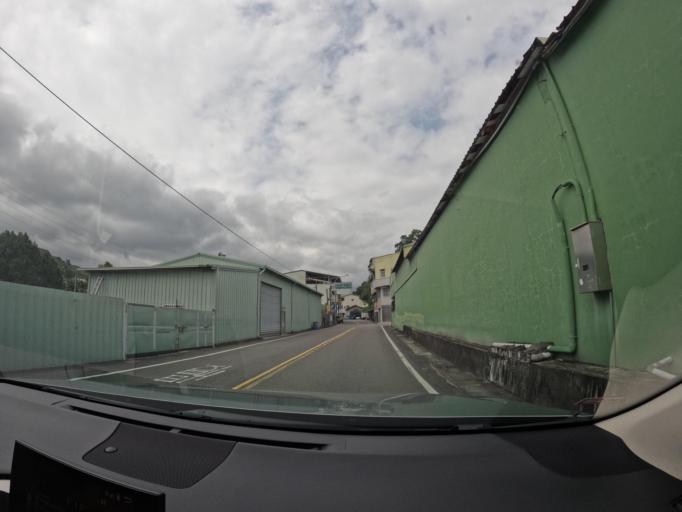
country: TW
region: Taiwan
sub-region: Miaoli
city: Miaoli
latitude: 24.3831
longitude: 120.8671
